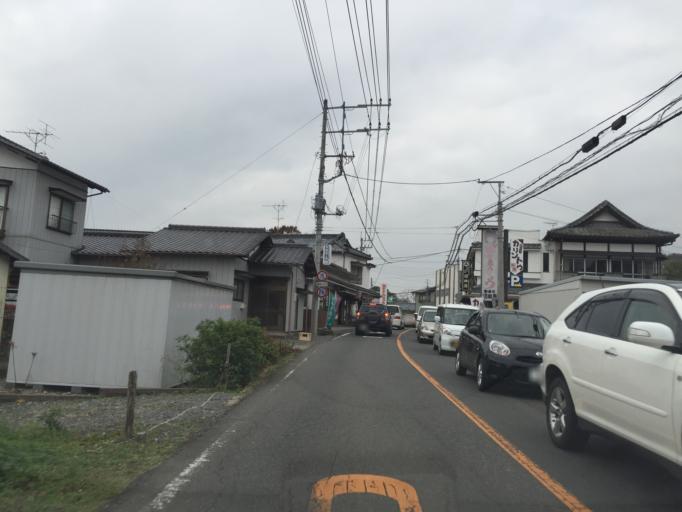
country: JP
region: Ibaraki
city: Tsukuba
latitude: 36.2078
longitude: 140.0829
